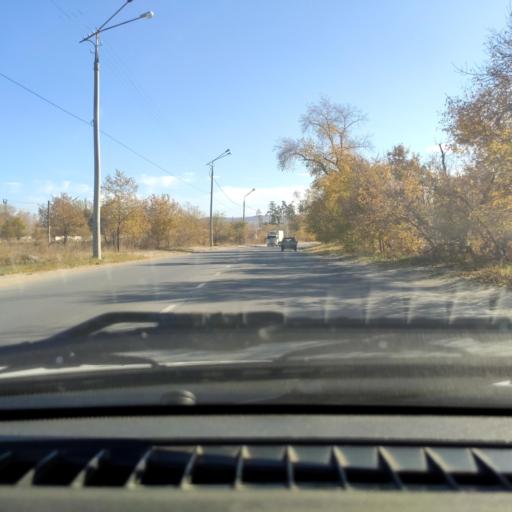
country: RU
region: Samara
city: Zhigulevsk
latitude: 53.4699
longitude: 49.5455
